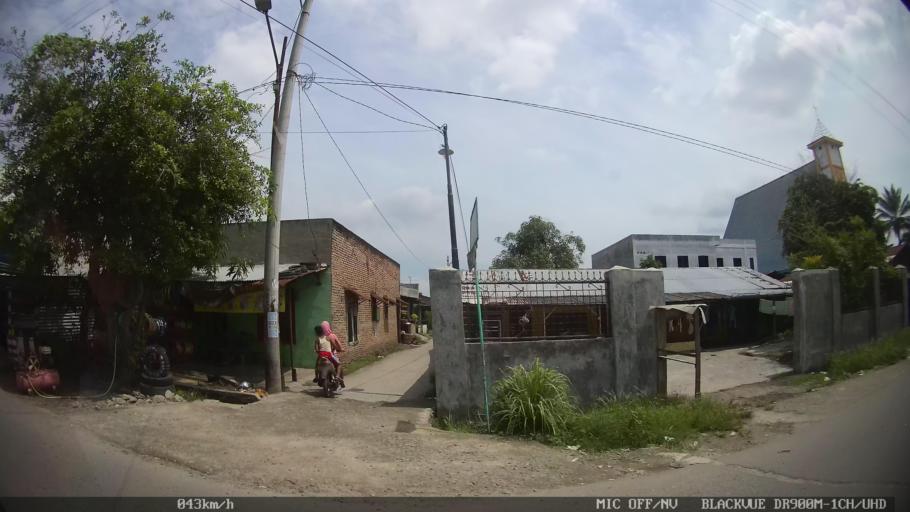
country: ID
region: North Sumatra
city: Medan
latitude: 3.6424
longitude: 98.6854
